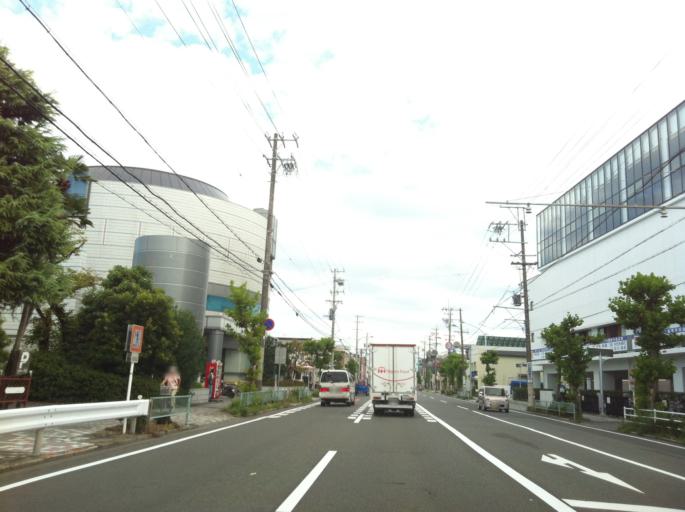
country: JP
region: Shizuoka
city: Shizuoka-shi
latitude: 35.0119
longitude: 138.4790
